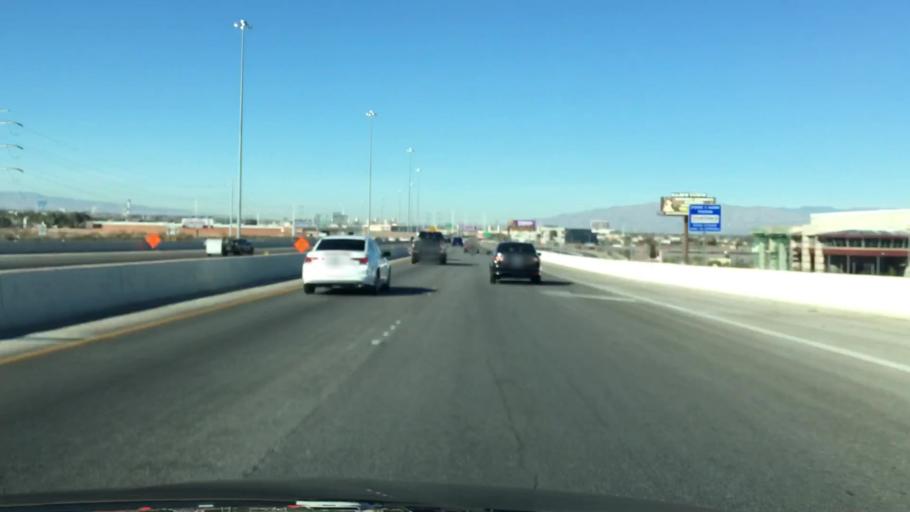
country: US
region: Nevada
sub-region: Clark County
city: Whitney
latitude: 36.0744
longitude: -115.0375
